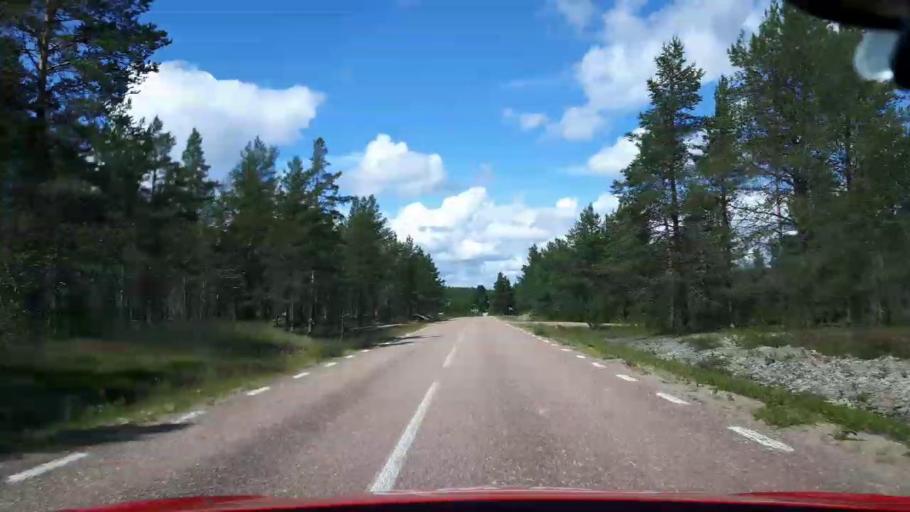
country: SE
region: Dalarna
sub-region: Alvdalens Kommun
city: AElvdalen
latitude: 61.8207
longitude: 13.5737
